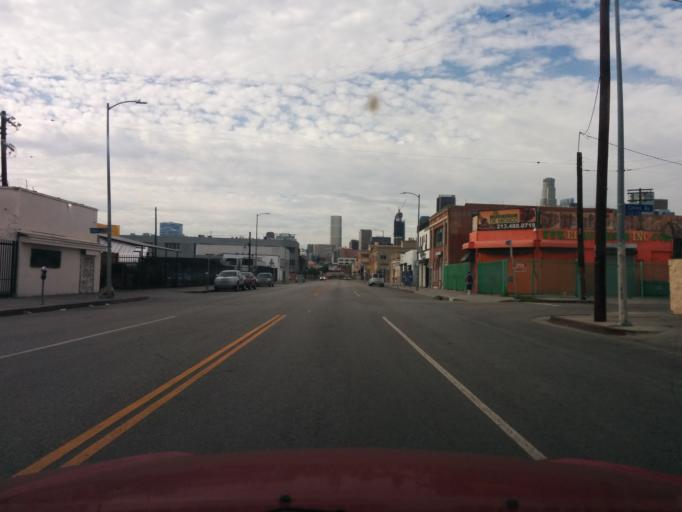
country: US
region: California
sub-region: Los Angeles County
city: Los Angeles
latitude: 34.0353
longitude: -118.2453
